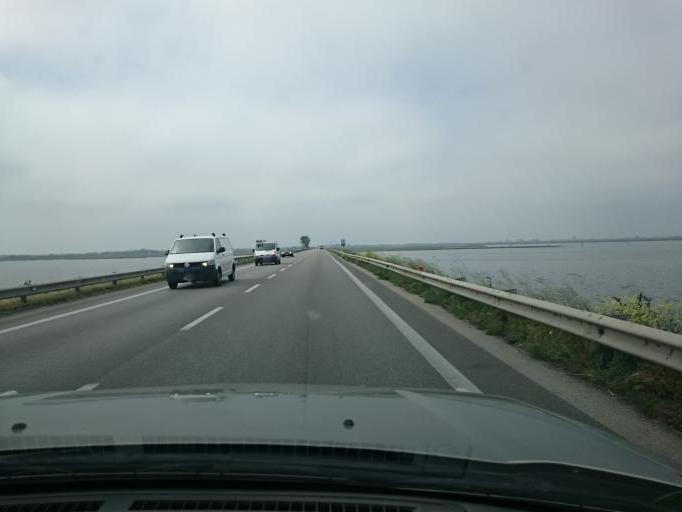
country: IT
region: Veneto
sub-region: Provincia di Venezia
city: Valli
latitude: 45.2129
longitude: 12.2302
